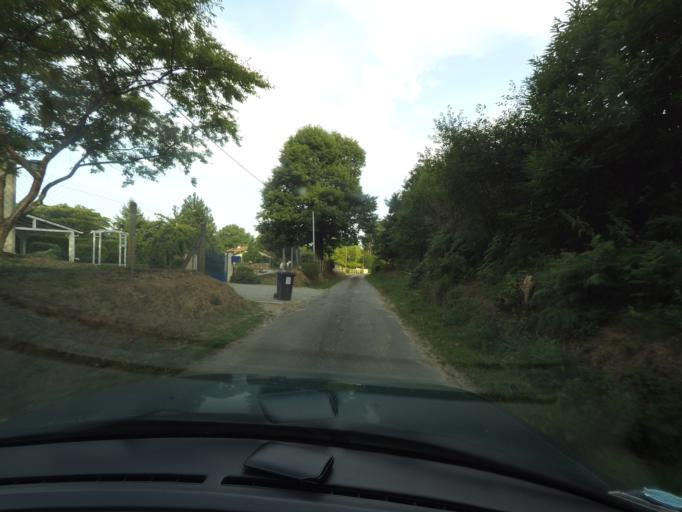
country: FR
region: Limousin
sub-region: Departement de la Haute-Vienne
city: Saint-Priest-sous-Aixe
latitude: 45.8142
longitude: 1.0751
